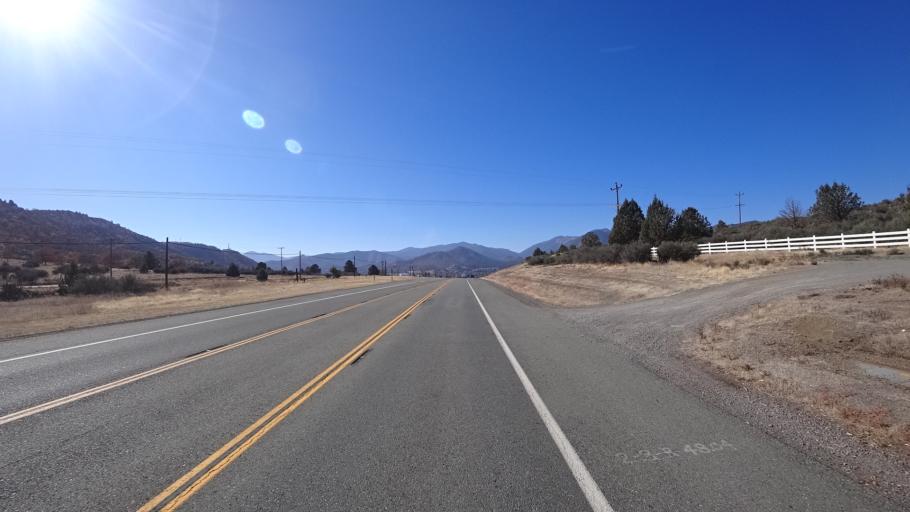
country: US
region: California
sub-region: Siskiyou County
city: Yreka
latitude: 41.7394
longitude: -122.6156
